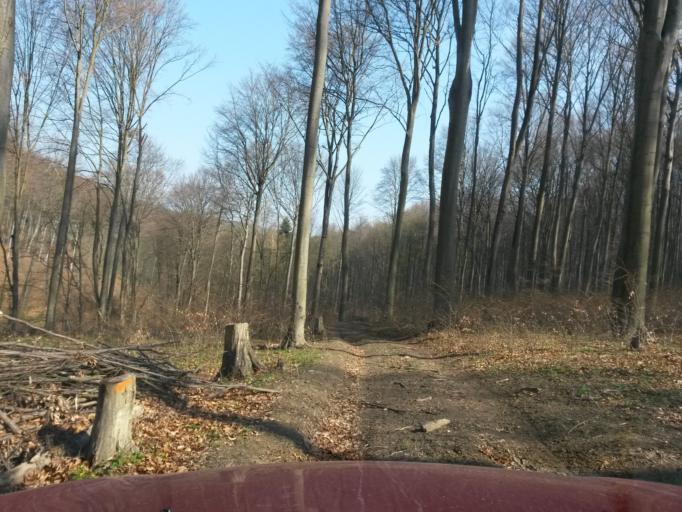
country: SK
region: Presovsky
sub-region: Okres Presov
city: Presov
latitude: 48.9299
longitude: 21.1471
